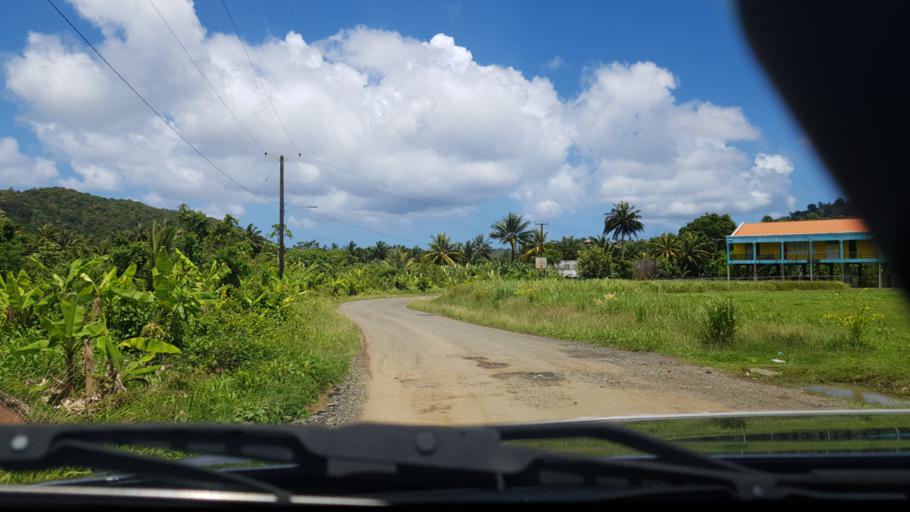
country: LC
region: Anse-la-Raye
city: Anse La Raye
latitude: 13.9491
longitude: -60.9939
